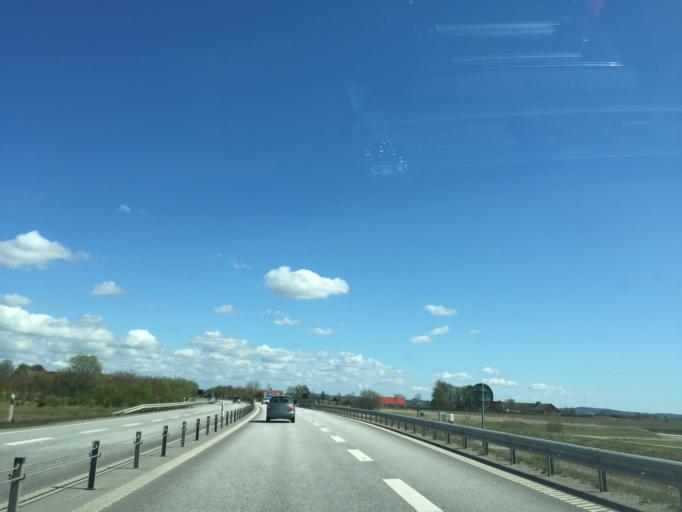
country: SE
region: Skane
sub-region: Svedala Kommun
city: Klagerup
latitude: 55.6434
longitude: 13.2653
